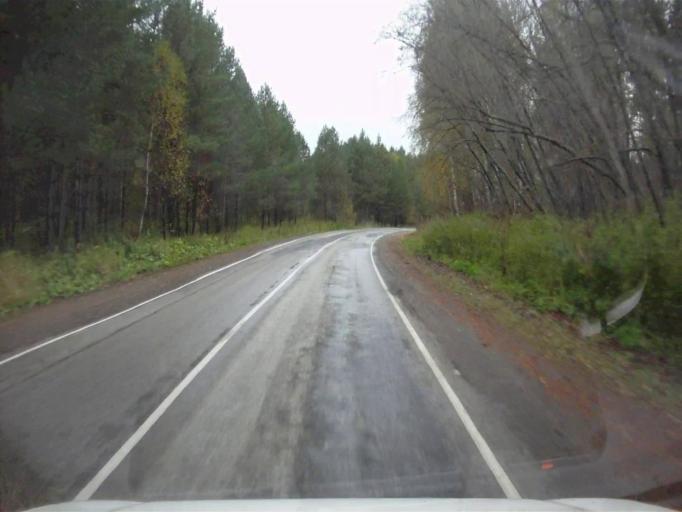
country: RU
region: Chelyabinsk
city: Nyazepetrovsk
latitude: 56.0627
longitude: 59.7080
